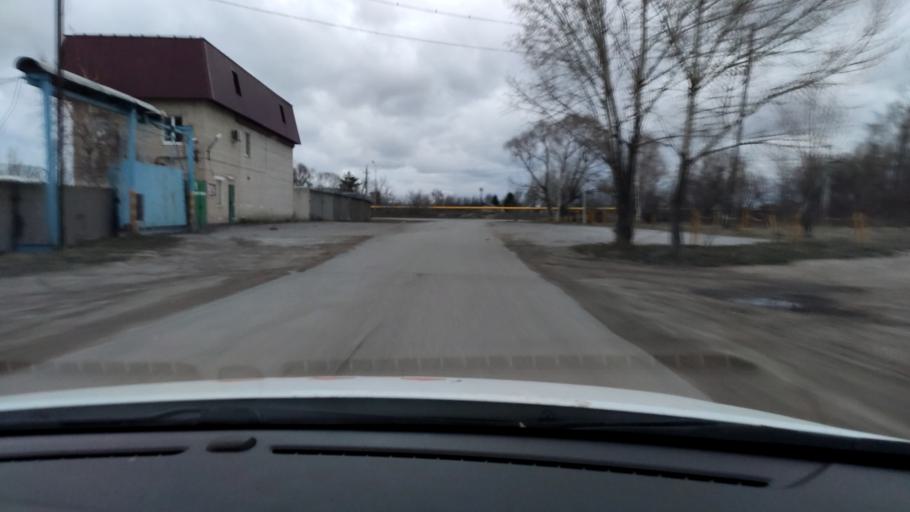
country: RU
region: Tatarstan
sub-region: Gorod Kazan'
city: Kazan
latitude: 55.7252
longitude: 49.1005
